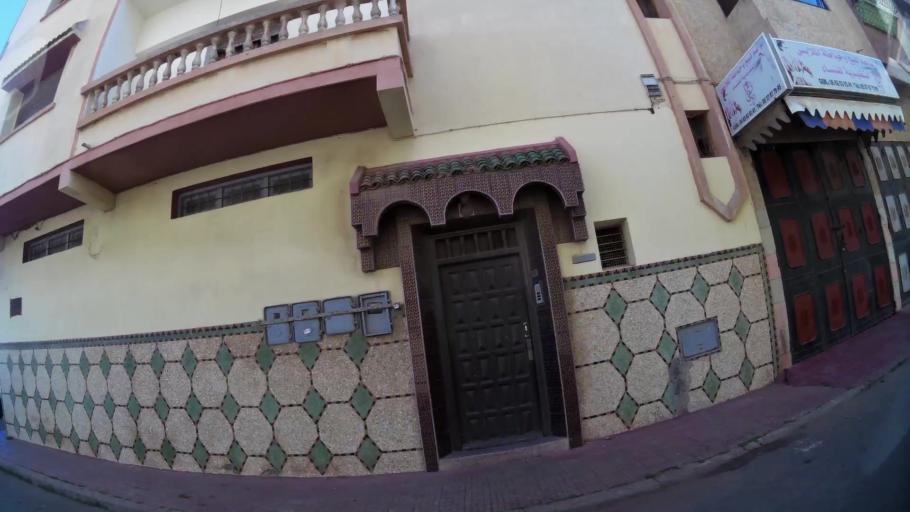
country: MA
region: Rabat-Sale-Zemmour-Zaer
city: Sale
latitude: 34.0690
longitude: -6.7986
